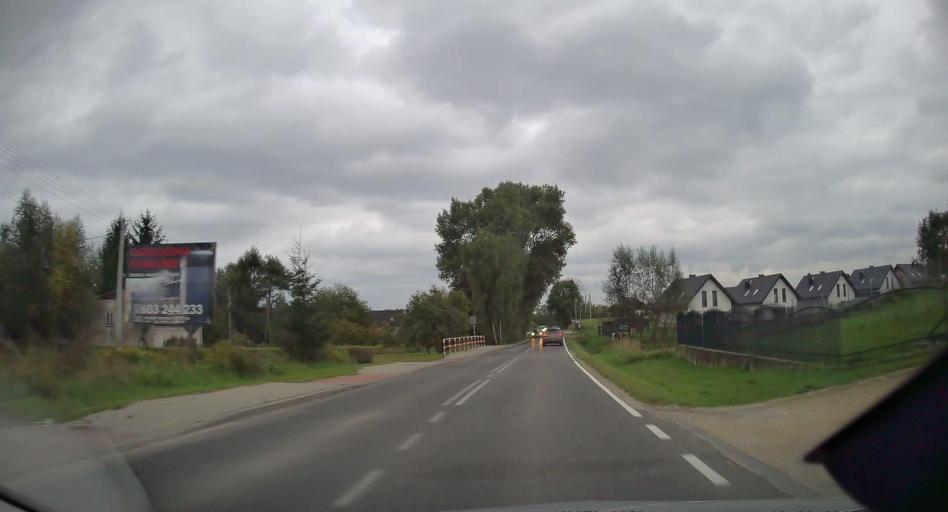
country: PL
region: Lesser Poland Voivodeship
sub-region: Powiat krakowski
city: Slomniki
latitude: 50.1591
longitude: 20.1038
